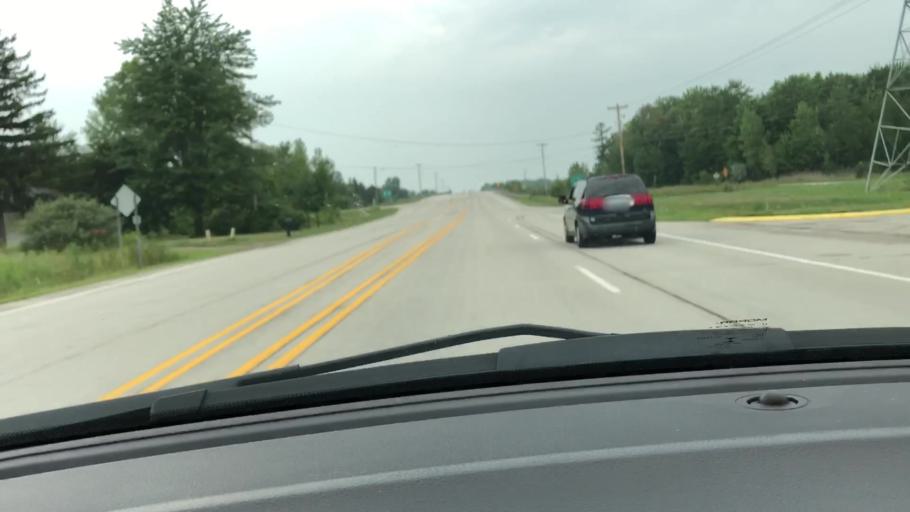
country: US
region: Michigan
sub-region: Bay County
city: Auburn
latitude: 43.6047
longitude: -84.1542
